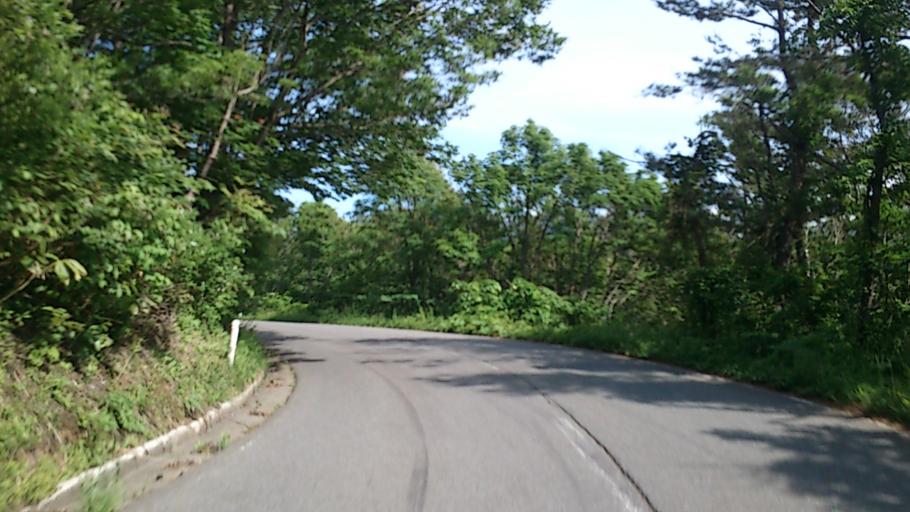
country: JP
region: Aomori
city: Aomori Shi
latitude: 40.7140
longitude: 140.8229
